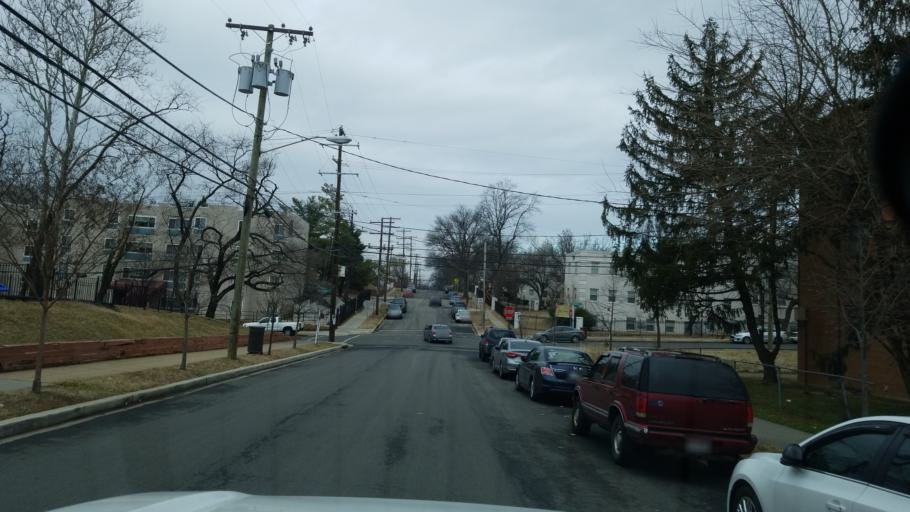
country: US
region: Maryland
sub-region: Prince George's County
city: Glassmanor
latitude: 38.8320
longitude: -76.9904
